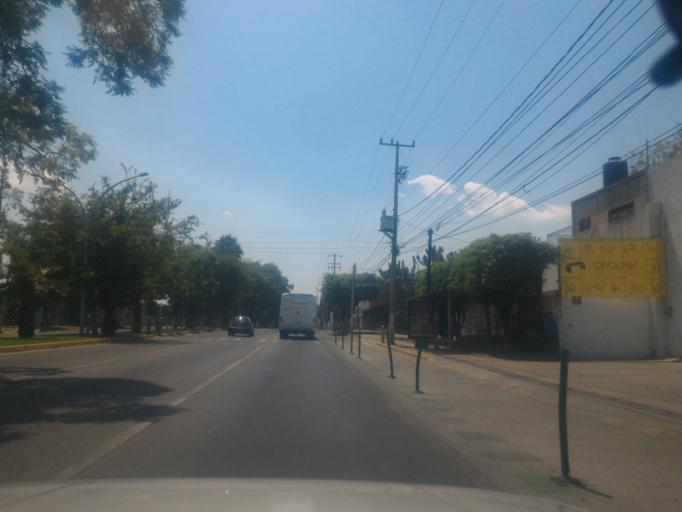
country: MX
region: Jalisco
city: Guadalajara
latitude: 20.6622
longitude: -103.3634
